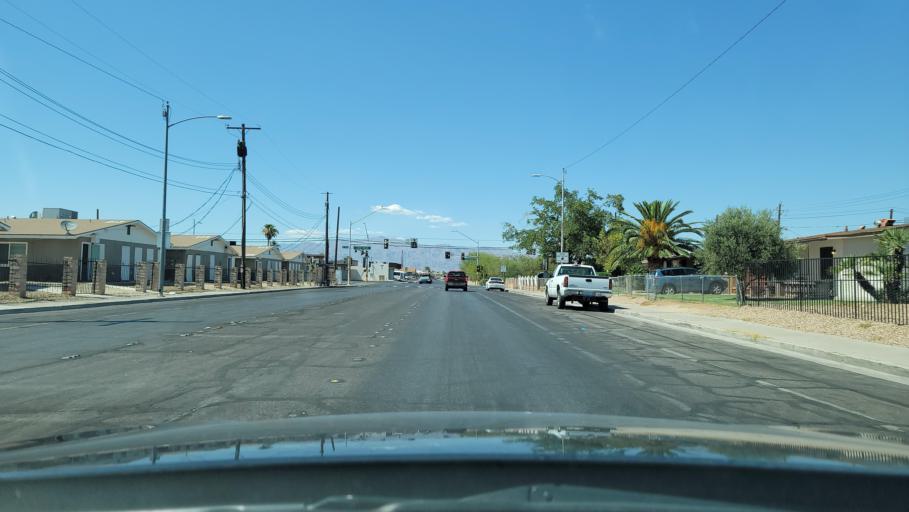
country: US
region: Nevada
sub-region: Clark County
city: Las Vegas
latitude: 36.1946
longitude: -115.1518
